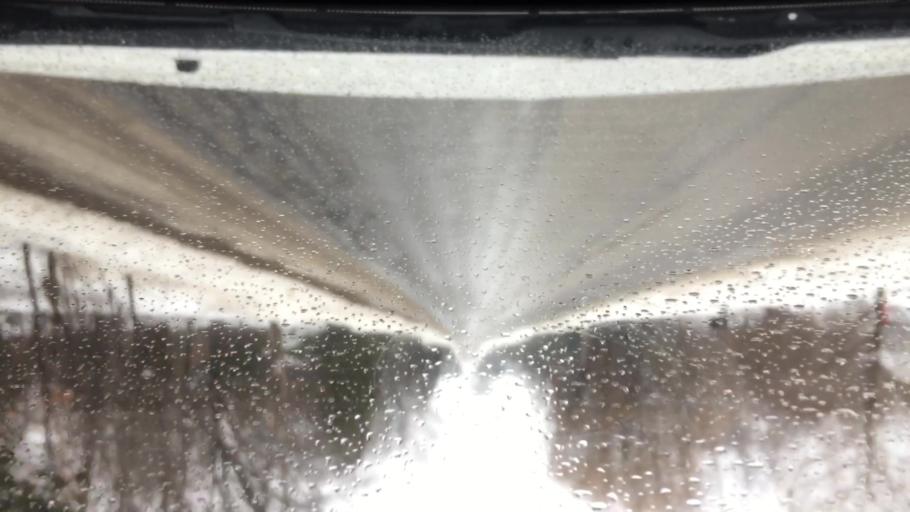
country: US
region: Michigan
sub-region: Charlevoix County
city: East Jordan
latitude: 45.1325
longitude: -85.1481
